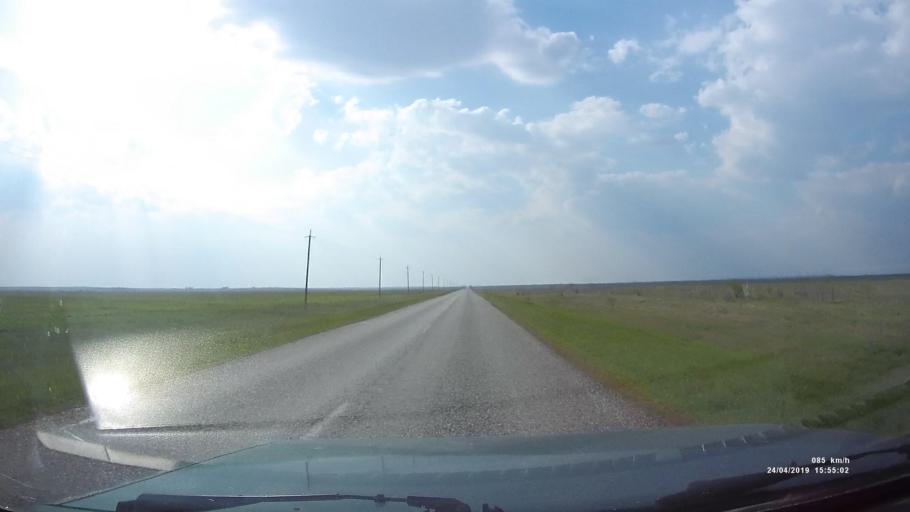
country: RU
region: Kalmykiya
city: Yashalta
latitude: 46.5876
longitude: 42.5572
